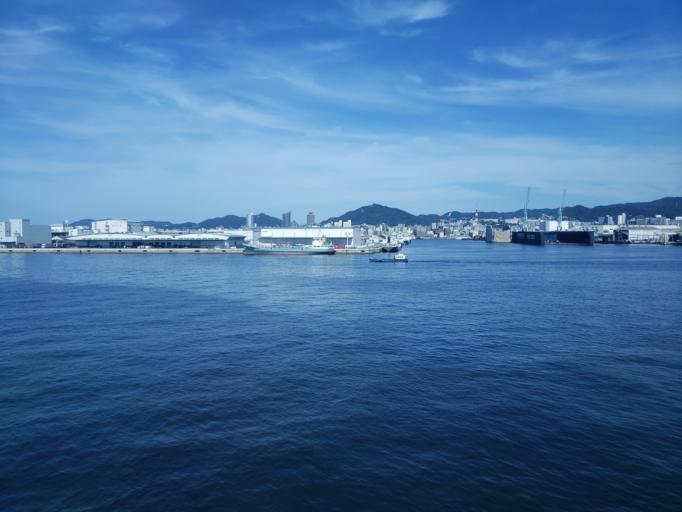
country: JP
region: Hyogo
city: Kobe
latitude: 34.6662
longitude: 135.1913
